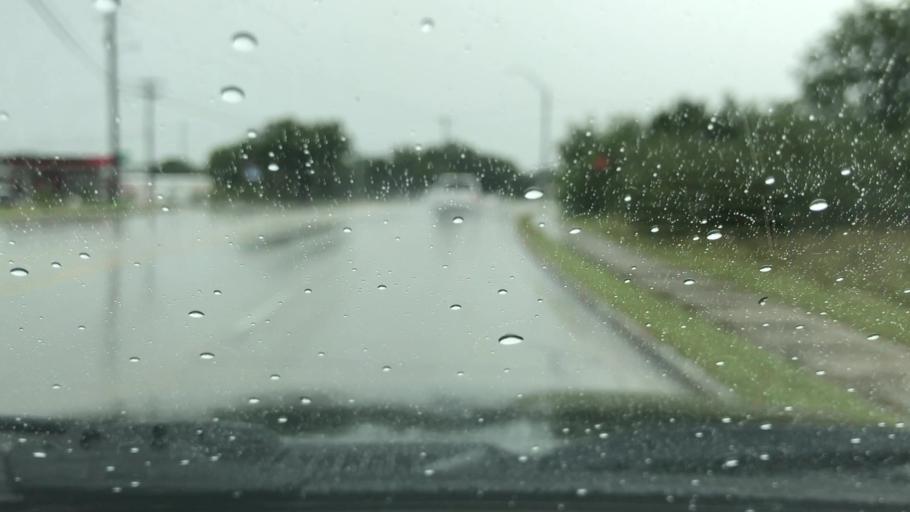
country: US
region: Texas
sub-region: Williamson County
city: Cedar Park
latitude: 30.4936
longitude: -97.8272
